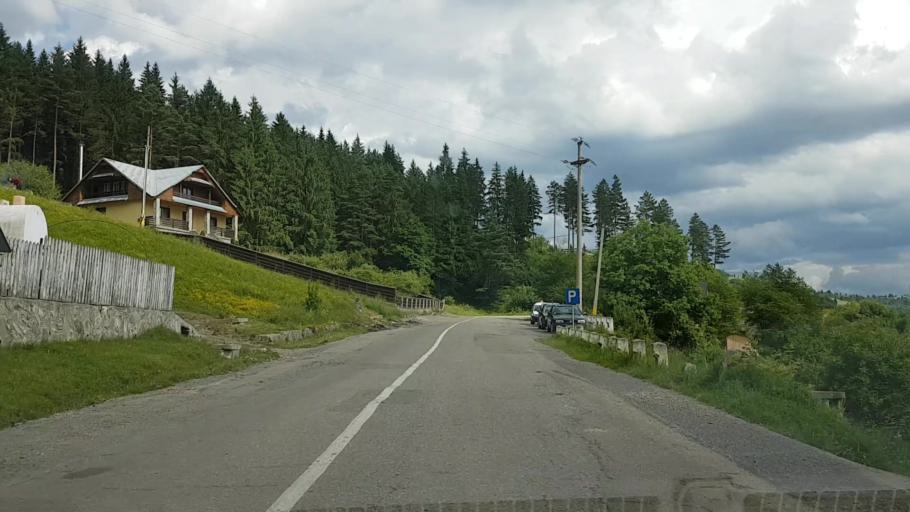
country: RO
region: Neamt
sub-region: Comuna Hangu
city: Hangu
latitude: 47.0096
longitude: 26.0883
